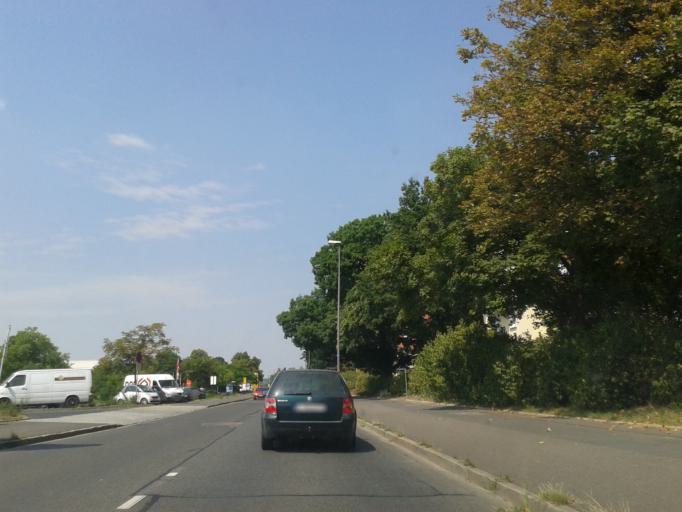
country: DE
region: Saxony
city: Radebeul
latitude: 51.0867
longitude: 13.6816
